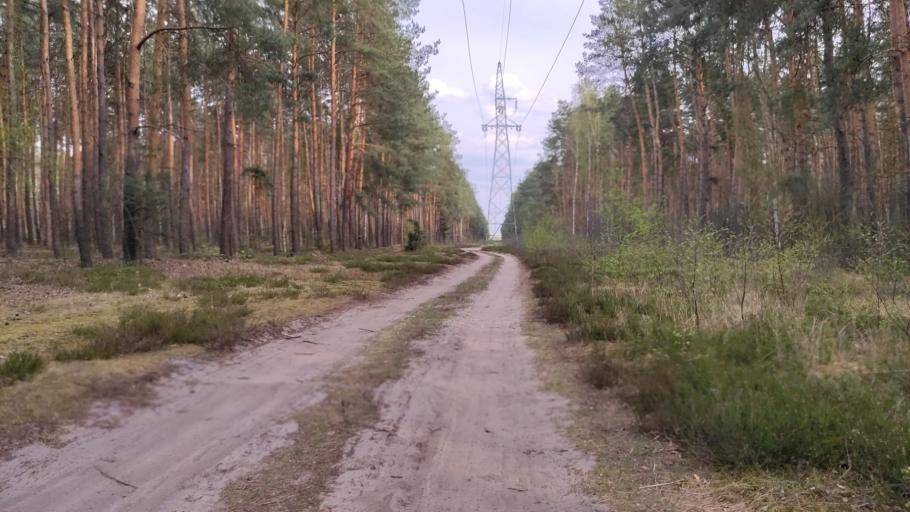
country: PL
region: Masovian Voivodeship
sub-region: Powiat grojecki
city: Warka
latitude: 51.7532
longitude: 21.1864
